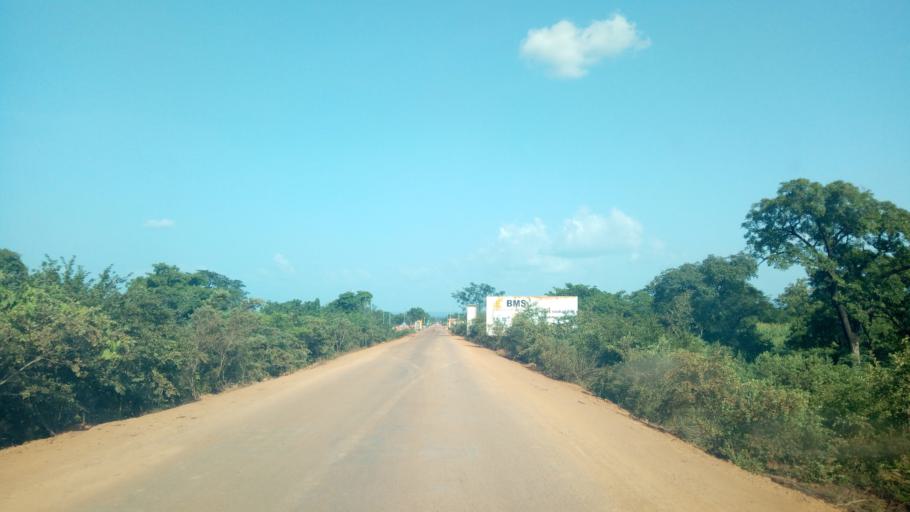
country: ML
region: Sikasso
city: Yorosso
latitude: 12.1851
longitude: -4.8332
